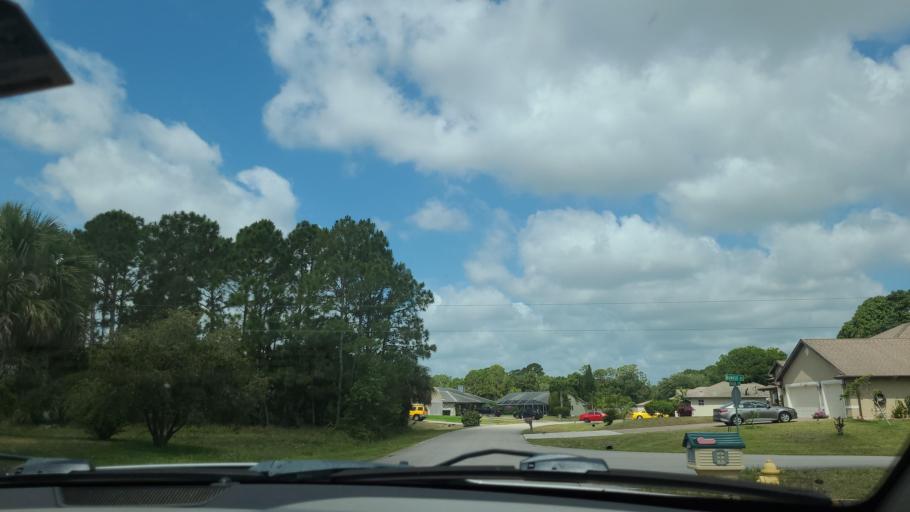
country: US
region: Florida
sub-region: Brevard County
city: Grant-Valkaria
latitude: 27.9656
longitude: -80.6691
